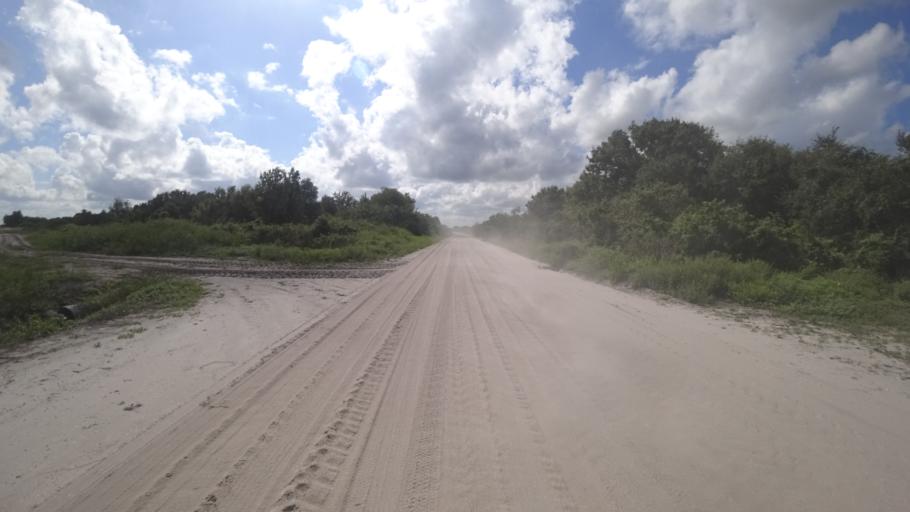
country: US
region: Florida
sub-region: Hillsborough County
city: Wimauma
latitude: 27.4443
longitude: -82.1826
